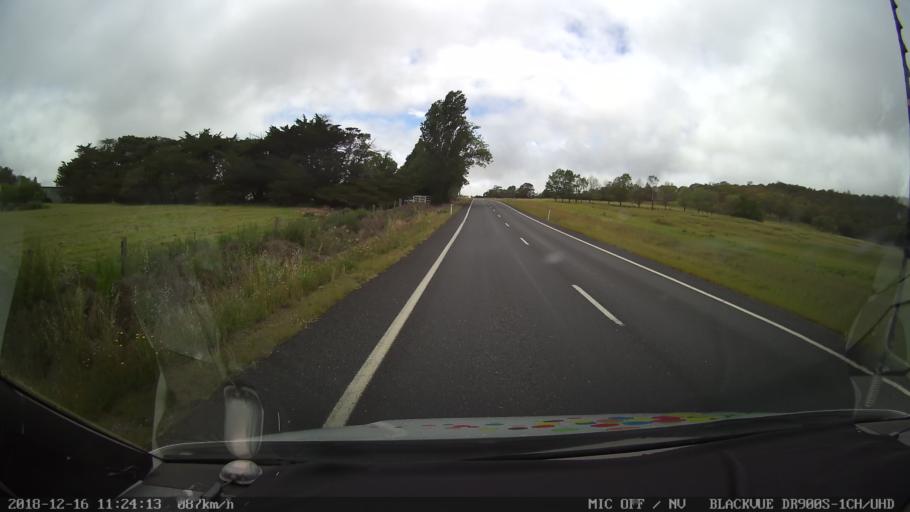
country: AU
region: New South Wales
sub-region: Tenterfield Municipality
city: Carrolls Creek
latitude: -29.0574
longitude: 152.0452
